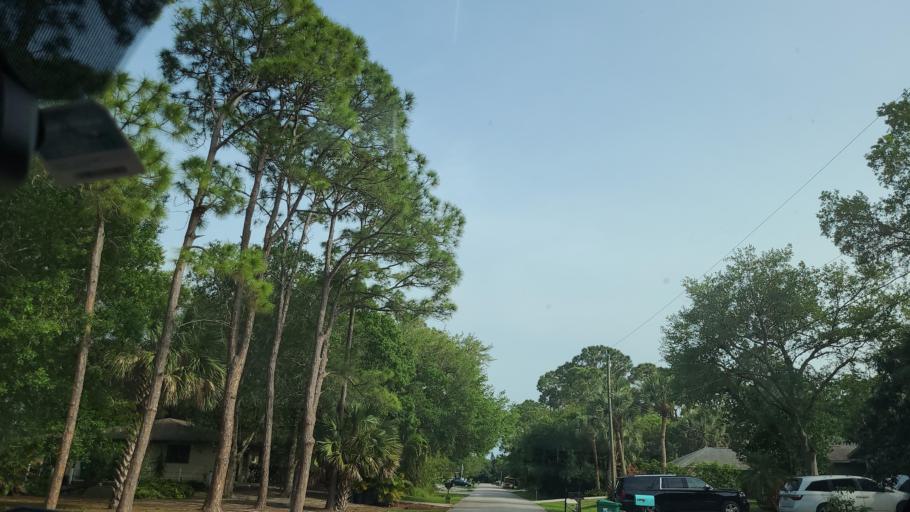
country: US
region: Florida
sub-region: Indian River County
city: Sebastian
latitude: 27.7674
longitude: -80.4905
